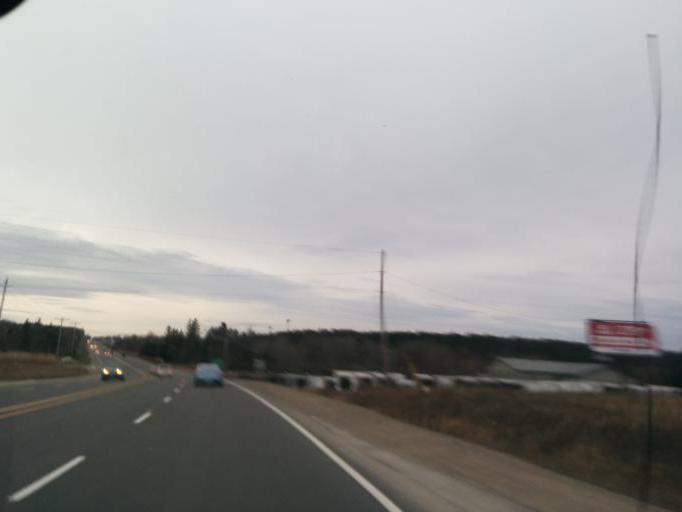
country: CA
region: Ontario
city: Shelburne
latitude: 44.0853
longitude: -80.1694
